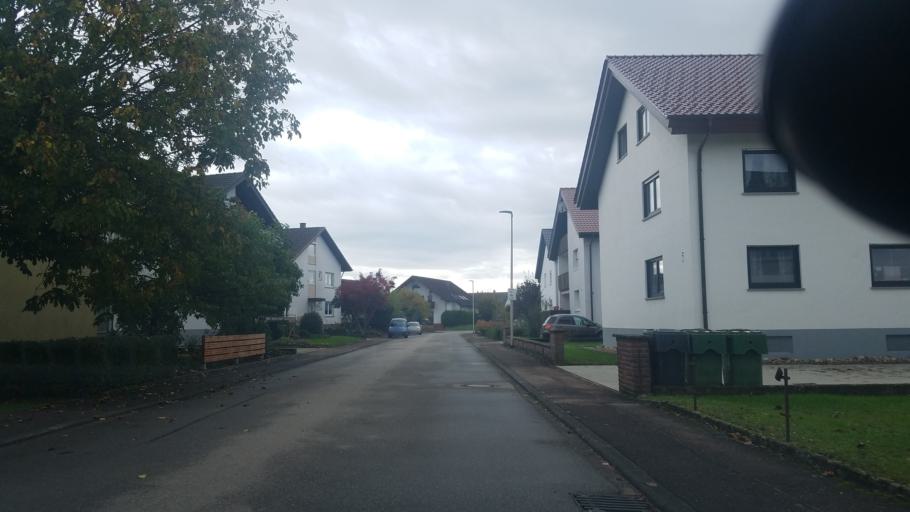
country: DE
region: Baden-Wuerttemberg
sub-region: Karlsruhe Region
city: Zell
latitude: 48.6568
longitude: 8.0250
